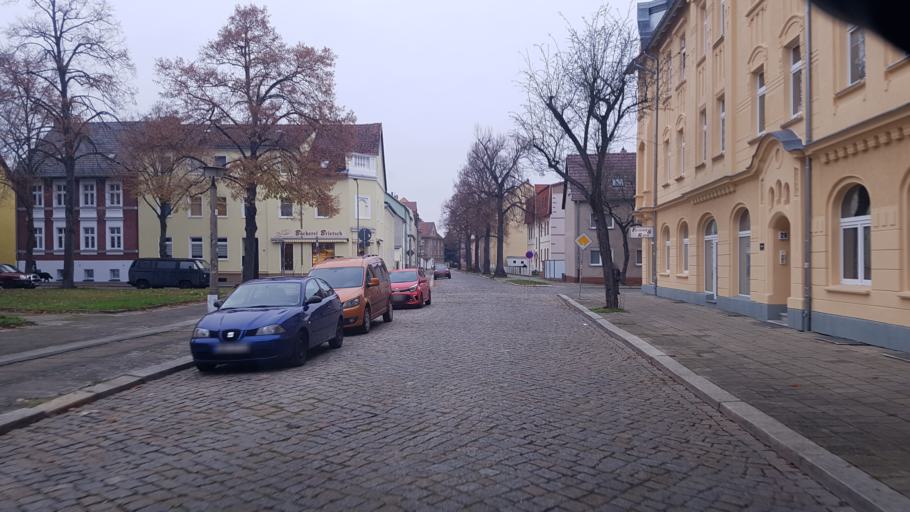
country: DE
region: Brandenburg
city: Guben
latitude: 51.9486
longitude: 14.7062
